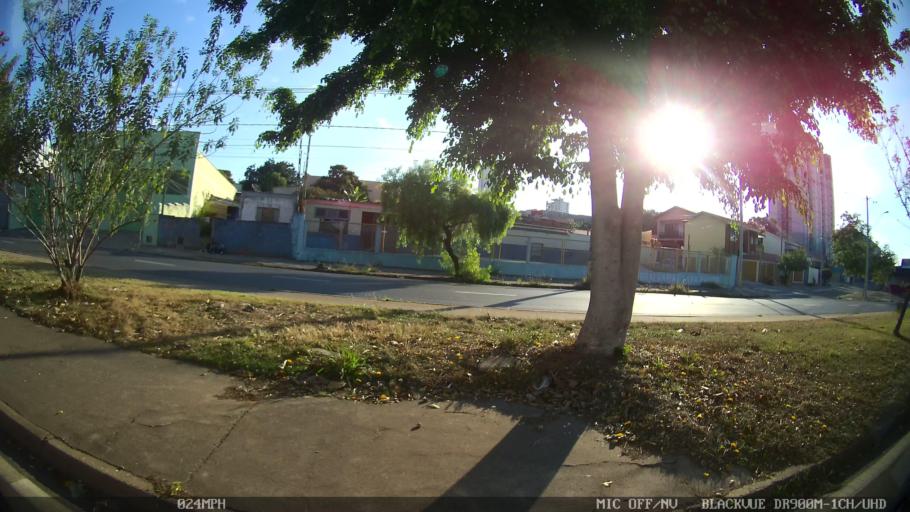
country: BR
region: Sao Paulo
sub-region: Piracicaba
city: Piracicaba
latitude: -22.7501
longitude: -47.6441
